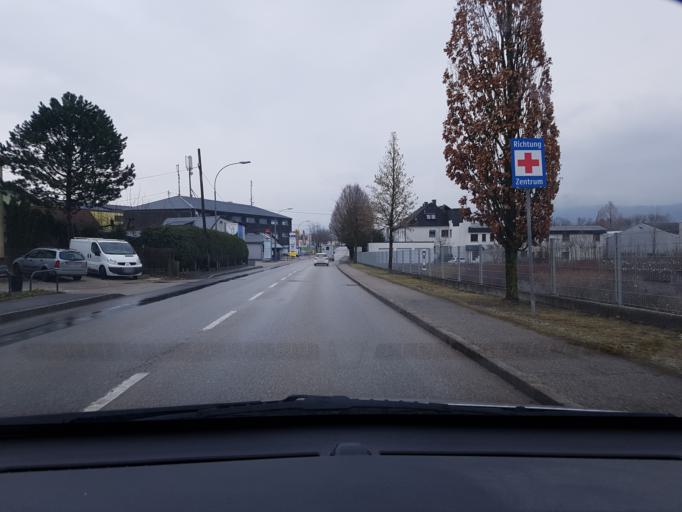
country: AT
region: Upper Austria
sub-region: Steyr Stadt
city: Steyr
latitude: 48.0502
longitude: 14.4003
